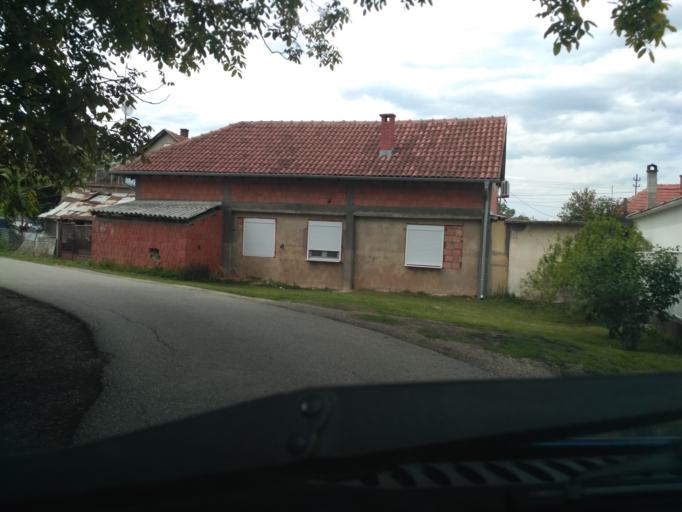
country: RS
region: Central Serbia
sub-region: Pomoravski Okrug
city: Svilajnac
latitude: 44.2307
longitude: 21.2047
